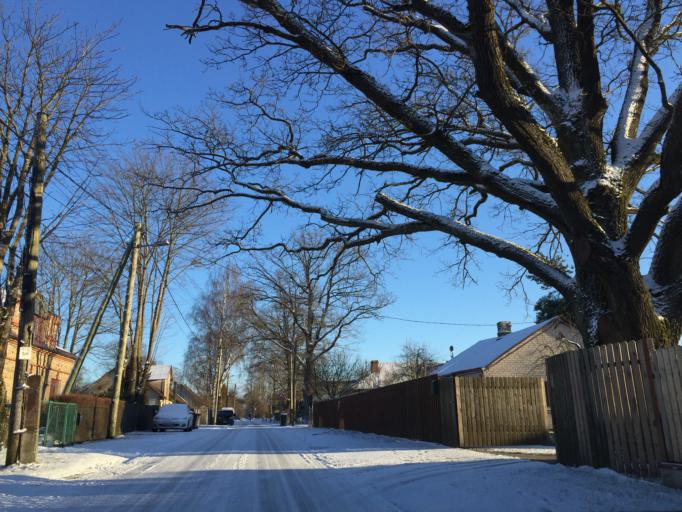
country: LV
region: Marupe
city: Marupe
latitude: 56.9116
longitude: 24.0552
